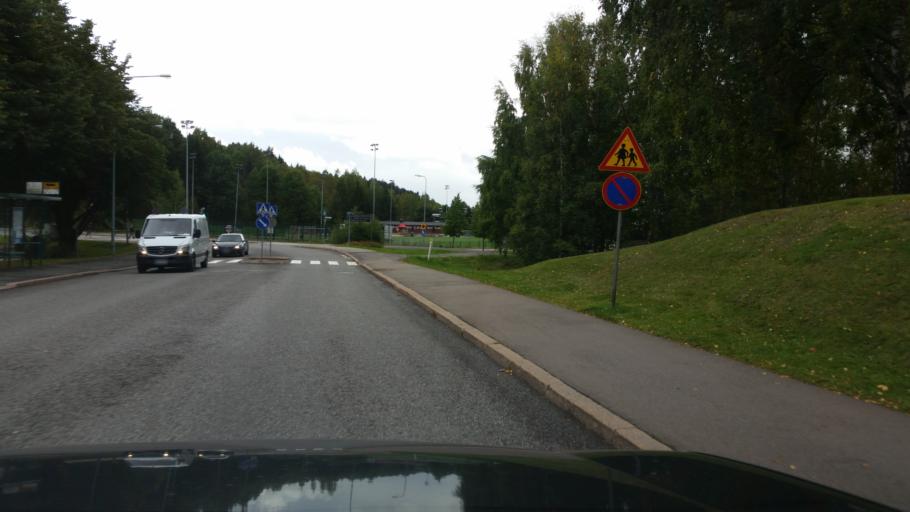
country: FI
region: Uusimaa
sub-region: Helsinki
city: Vantaa
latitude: 60.2400
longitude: 25.0027
